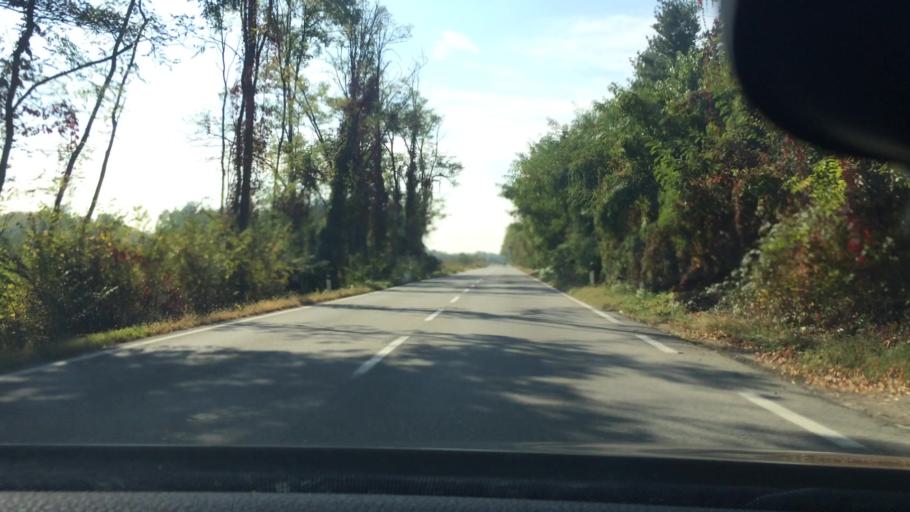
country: IT
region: Lombardy
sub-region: Citta metropolitana di Milano
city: Cerro Maggiore
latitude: 45.6091
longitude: 8.9737
